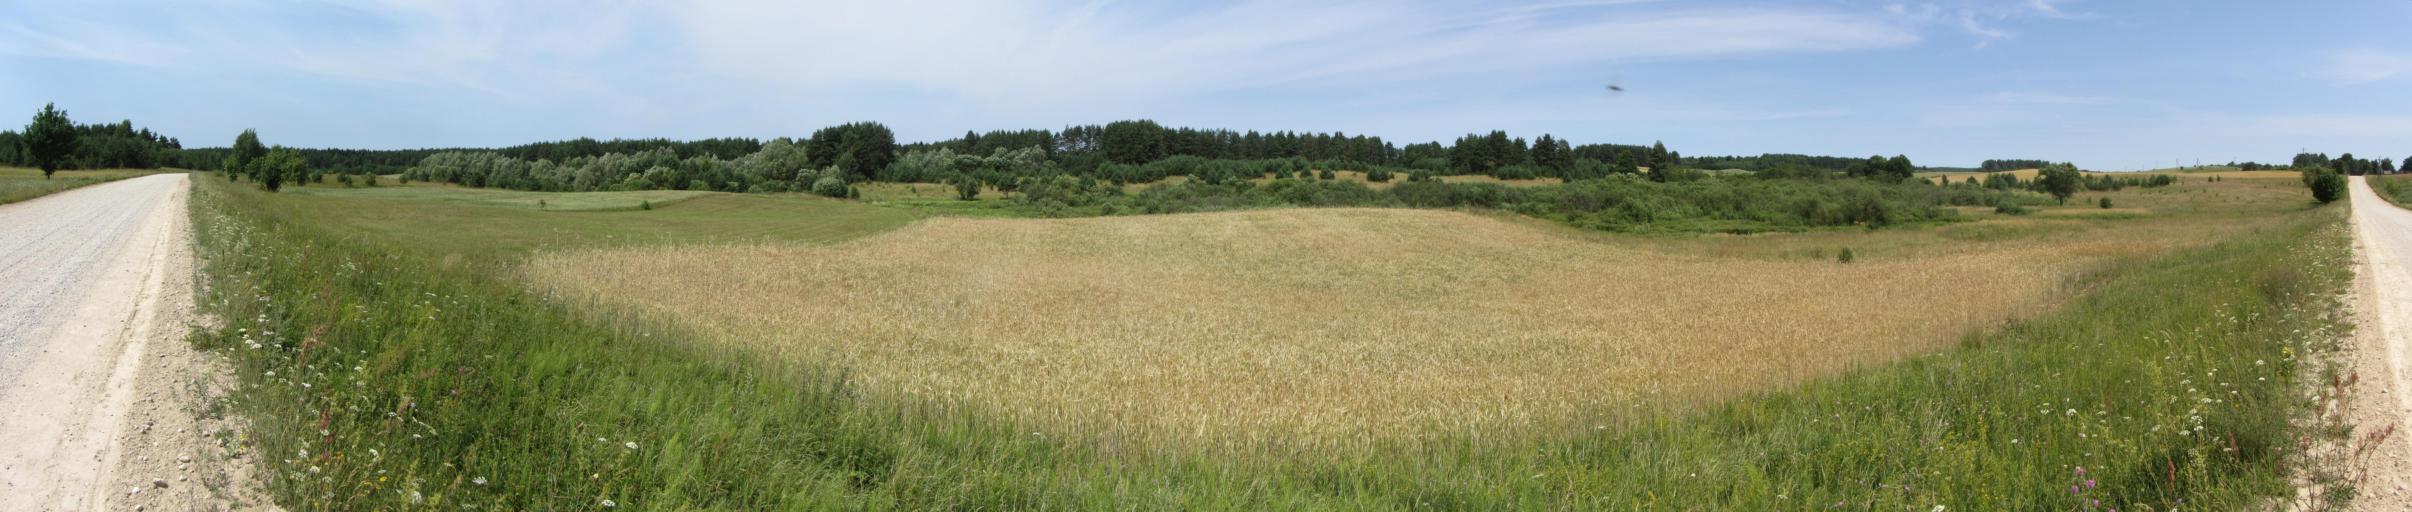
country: LT
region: Alytaus apskritis
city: Druskininkai
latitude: 54.1399
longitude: 23.9590
